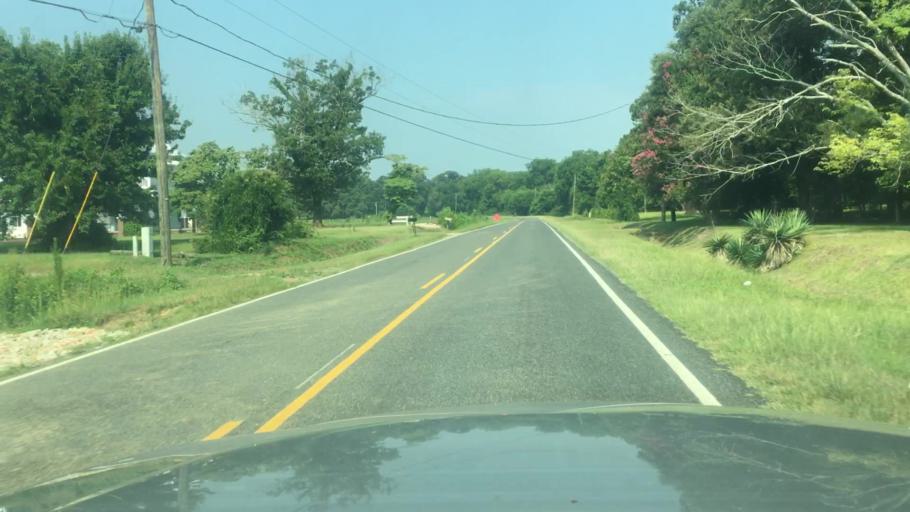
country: US
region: North Carolina
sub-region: Cumberland County
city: Hope Mills
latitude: 34.9091
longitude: -78.8662
